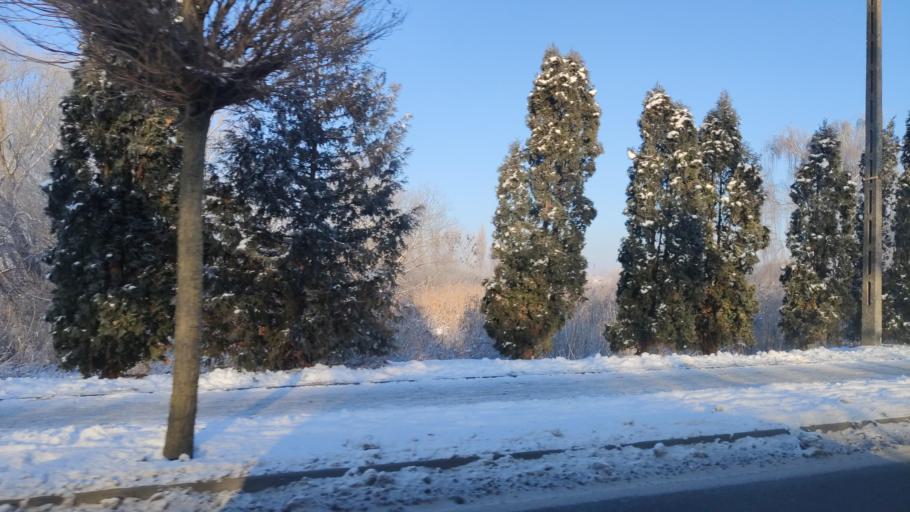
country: PL
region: Kujawsko-Pomorskie
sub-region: Powiat zninski
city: Barcin
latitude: 52.8603
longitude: 17.9452
